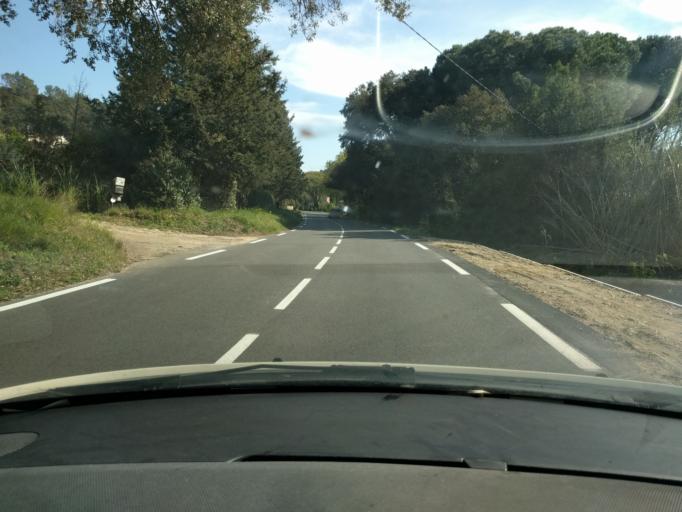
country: FR
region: Provence-Alpes-Cote d'Azur
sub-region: Departement du Var
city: La Crau
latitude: 43.1683
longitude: 6.1185
